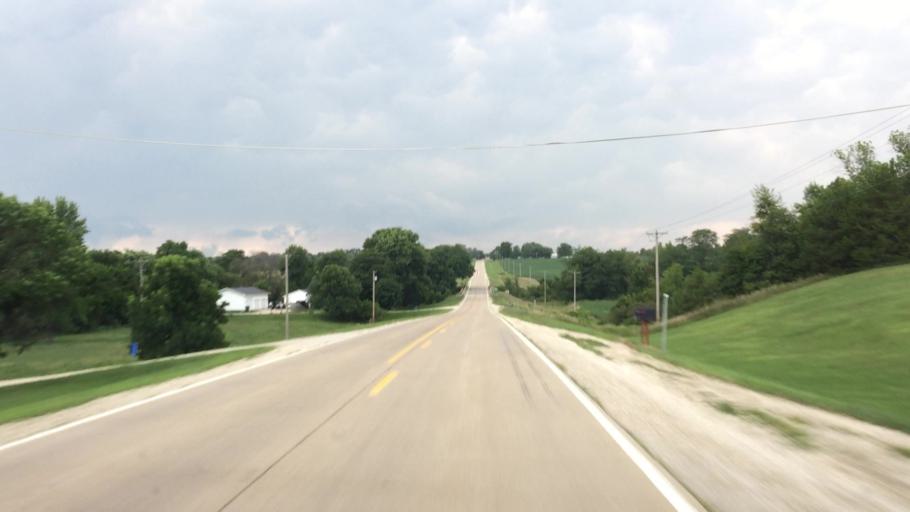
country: US
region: Iowa
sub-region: Lee County
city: Fort Madison
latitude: 40.7211
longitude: -91.3298
